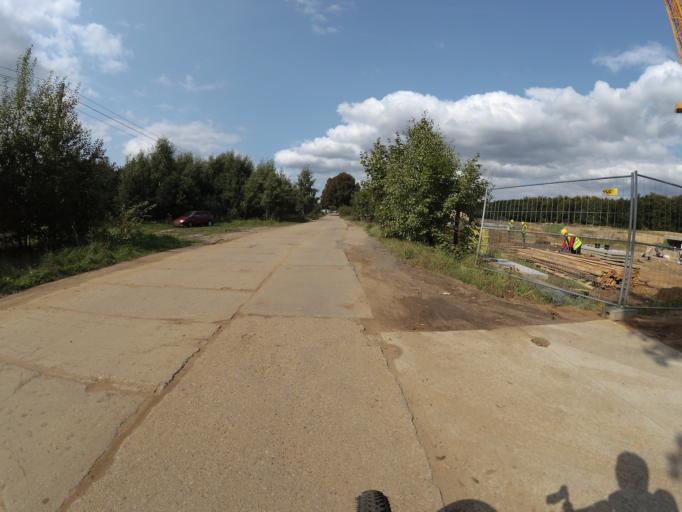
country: PL
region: Pomeranian Voivodeship
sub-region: Powiat wejherowski
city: Bojano
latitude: 54.4998
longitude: 18.4320
